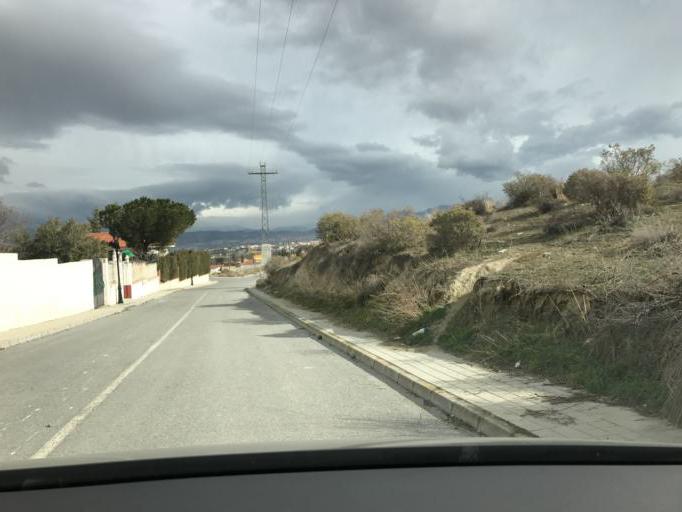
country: ES
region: Andalusia
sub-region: Provincia de Granada
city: Alhendin
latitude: 37.1044
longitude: -3.6692
